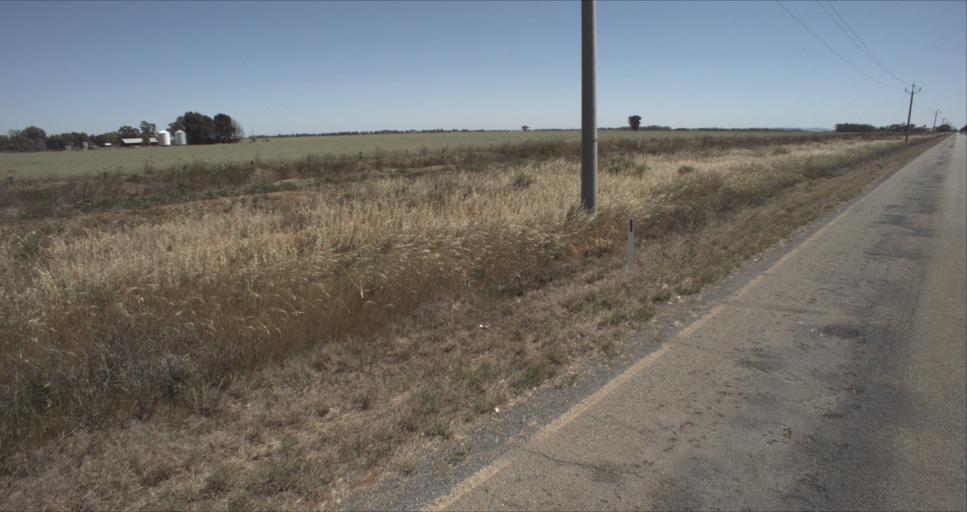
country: AU
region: New South Wales
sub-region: Leeton
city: Leeton
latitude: -34.5128
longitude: 146.2848
